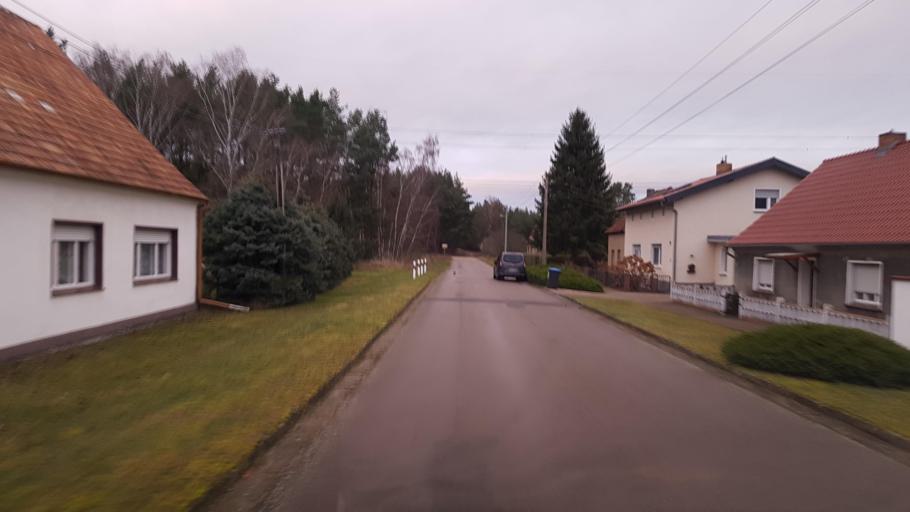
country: DE
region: Brandenburg
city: Luebben
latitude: 51.9089
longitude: 13.8062
